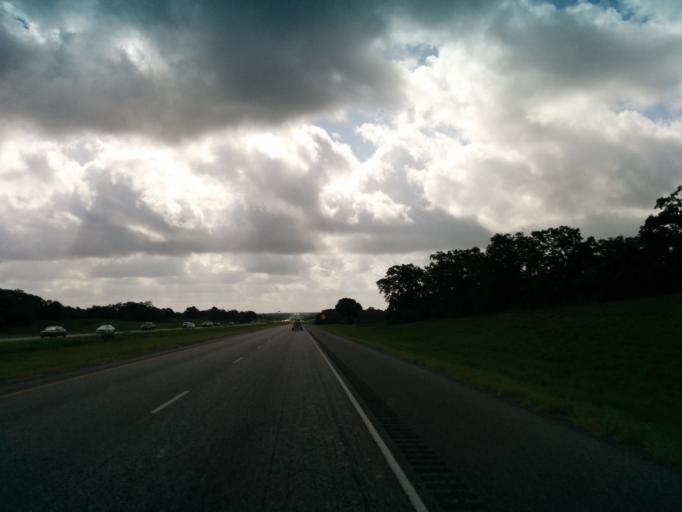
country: US
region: Texas
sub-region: Caldwell County
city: Luling
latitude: 29.6530
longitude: -97.5513
